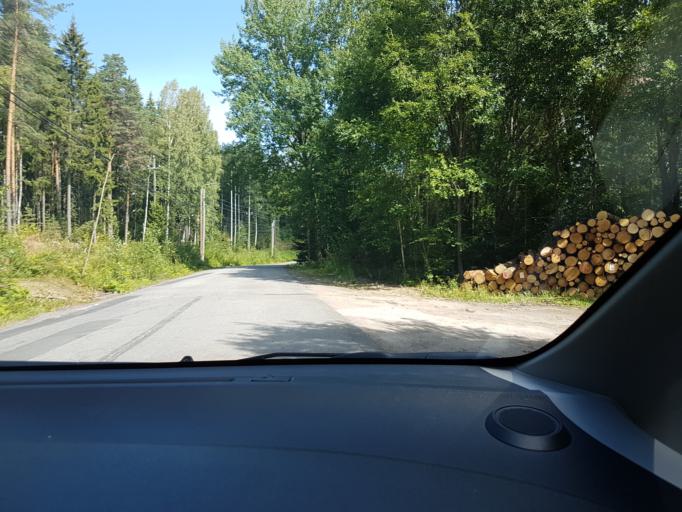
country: FI
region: Uusimaa
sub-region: Helsinki
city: Kilo
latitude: 60.3353
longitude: 24.7860
